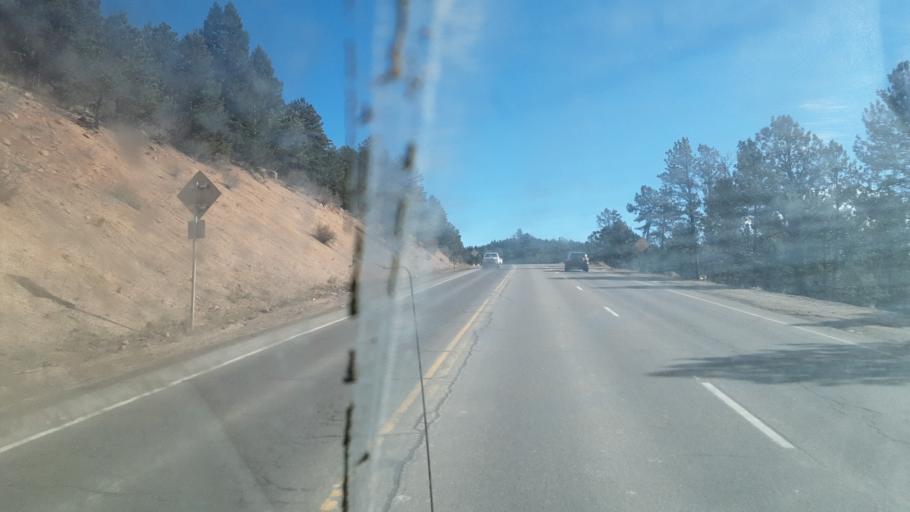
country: US
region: Colorado
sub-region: Jefferson County
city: Evergreen
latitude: 39.4542
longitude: -105.4343
